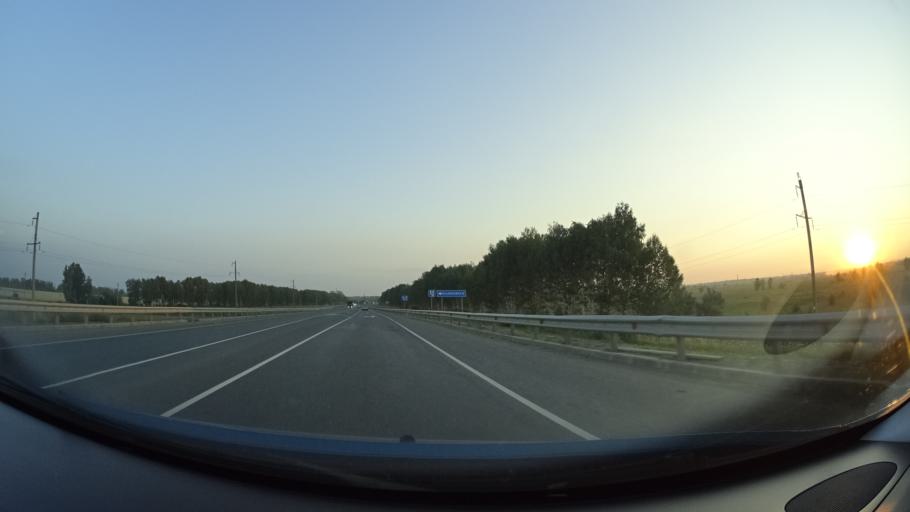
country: RU
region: Samara
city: Sernovodsk
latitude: 53.8953
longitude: 51.2677
